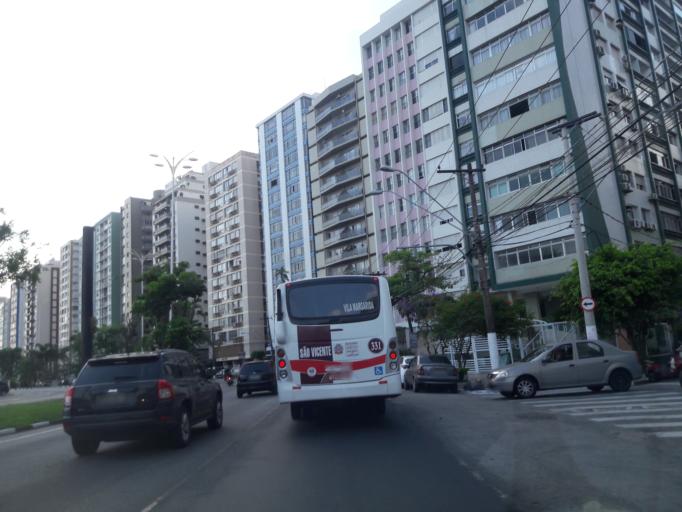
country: BR
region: Sao Paulo
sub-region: Sao Vicente
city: Sao Vicente
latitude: -23.9702
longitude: -46.3679
